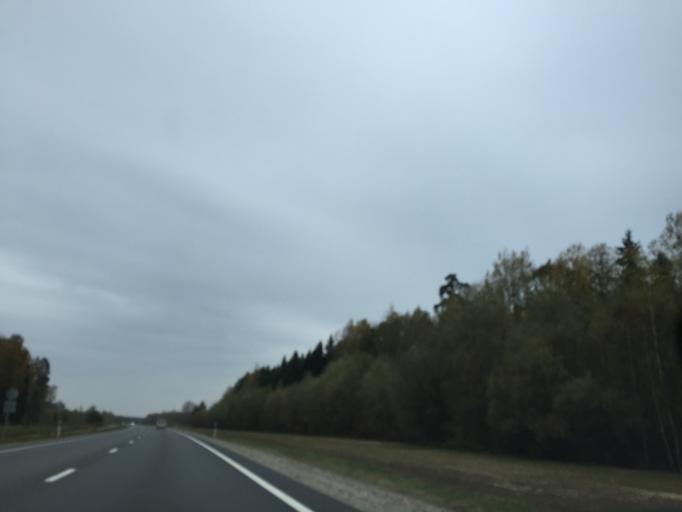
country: LV
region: Ozolnieku
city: Ozolnieki
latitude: 56.6836
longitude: 23.8209
